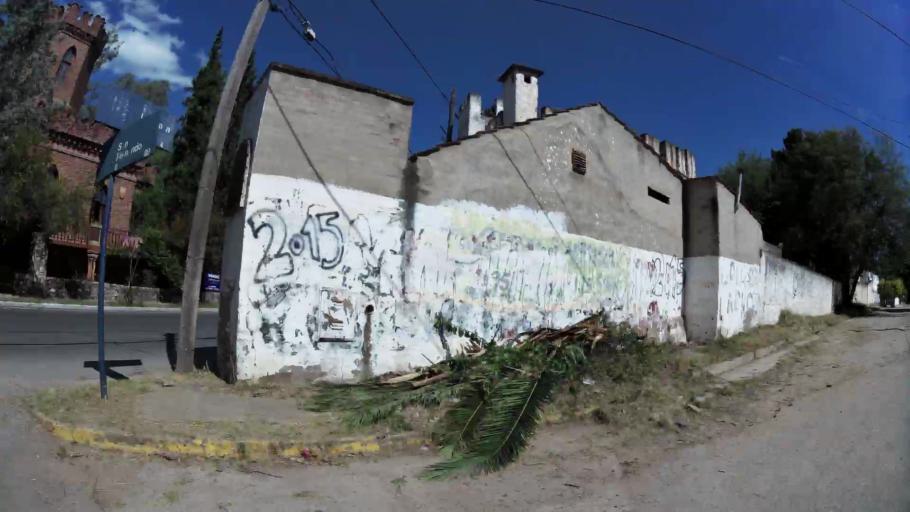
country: AR
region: Cordoba
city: Villa Allende
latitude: -31.2905
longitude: -64.2970
